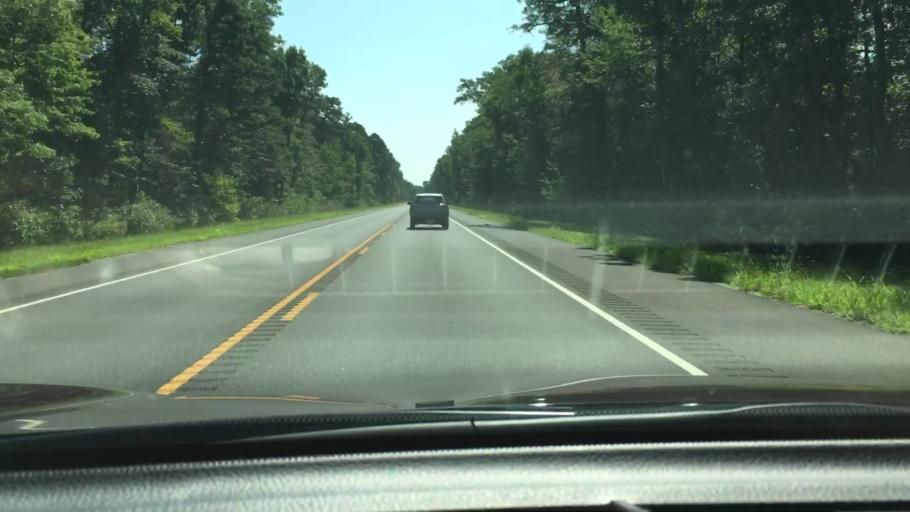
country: US
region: New Jersey
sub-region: Cape May County
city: Woodbine
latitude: 39.3152
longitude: -74.8323
